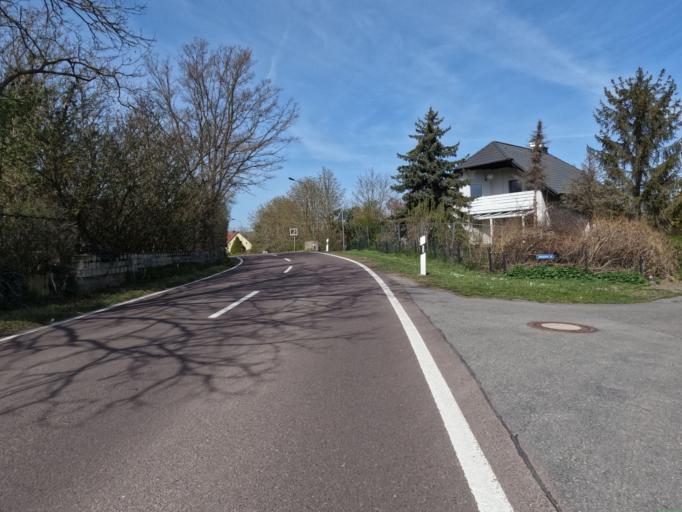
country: DE
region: Saxony-Anhalt
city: Wettin
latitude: 51.5782
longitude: 11.7725
